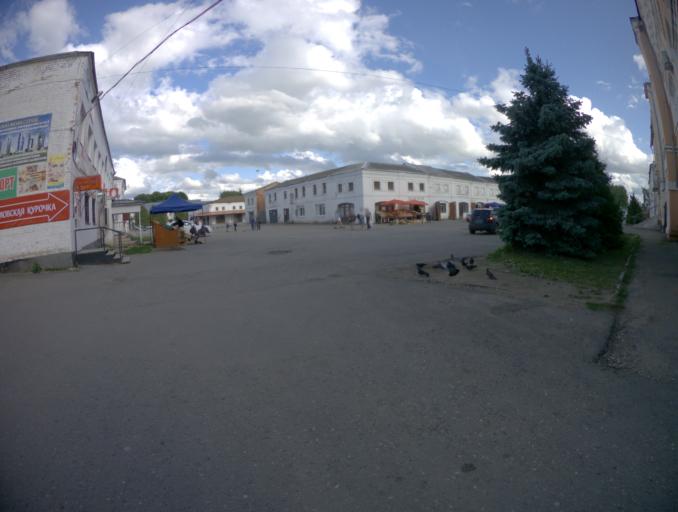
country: RU
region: Vladimir
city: Yur'yev-Pol'skiy
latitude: 56.5005
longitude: 39.6807
